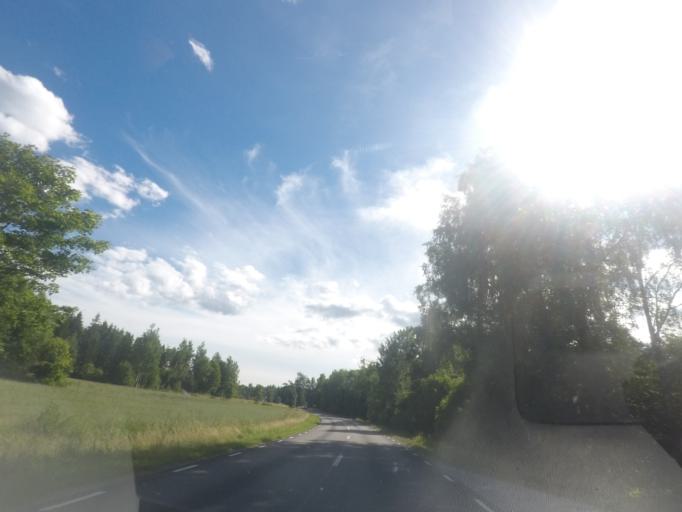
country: SE
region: Stockholm
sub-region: Norrtalje Kommun
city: Arno
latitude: 60.0023
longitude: 18.8006
